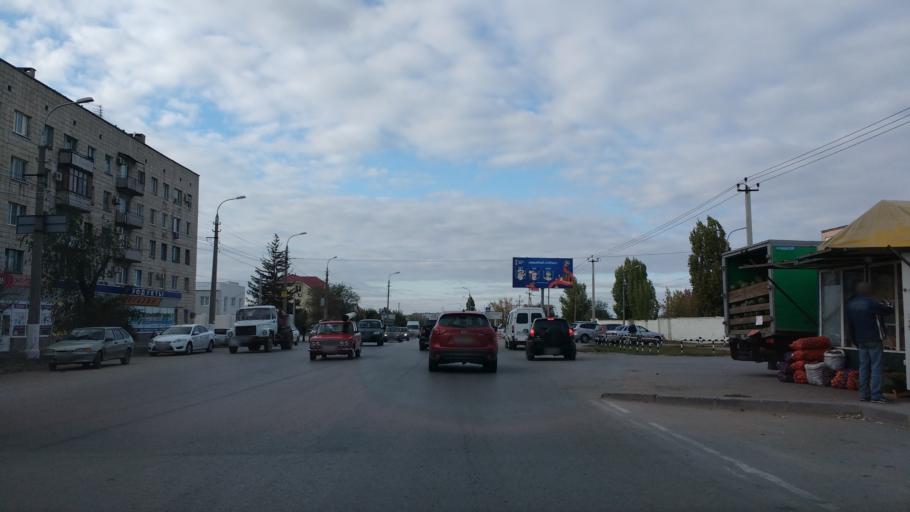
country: RU
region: Volgograd
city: Volgograd
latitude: 48.7667
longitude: 44.5289
